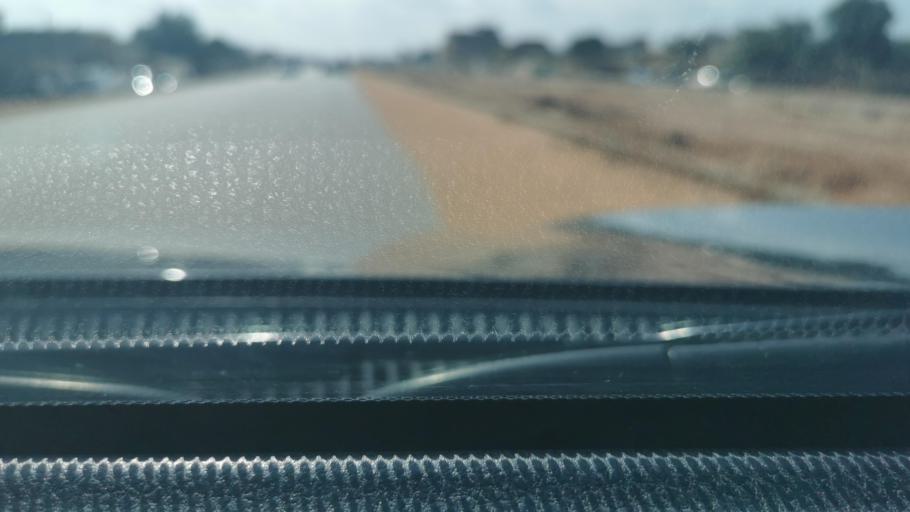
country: TG
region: Maritime
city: Lome
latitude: 6.2083
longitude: 1.1394
